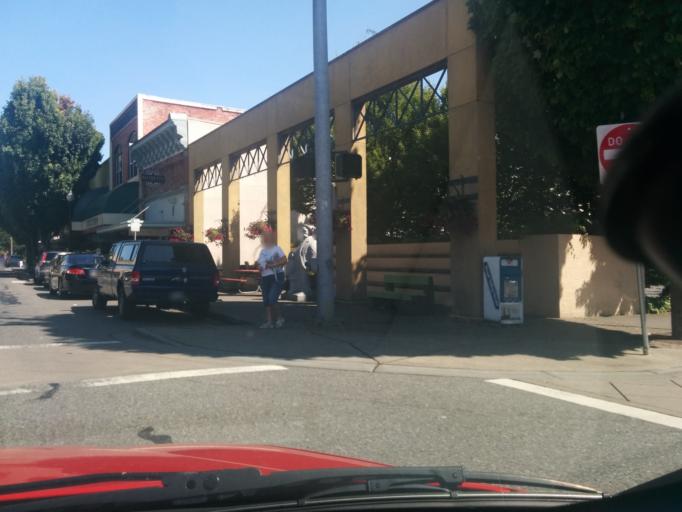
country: US
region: Washington
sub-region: Skagit County
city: Mount Vernon
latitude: 48.4194
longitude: -122.3378
